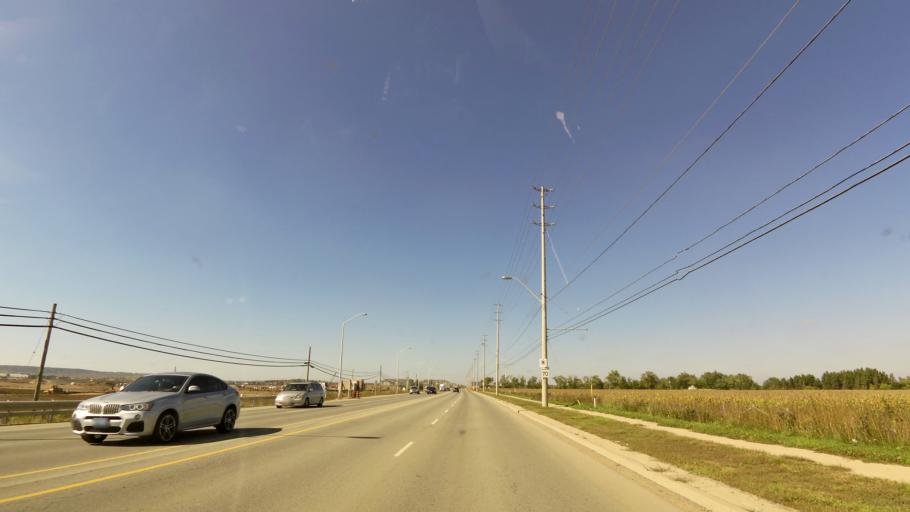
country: CA
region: Ontario
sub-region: Halton
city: Milton
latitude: 43.4905
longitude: -79.8397
